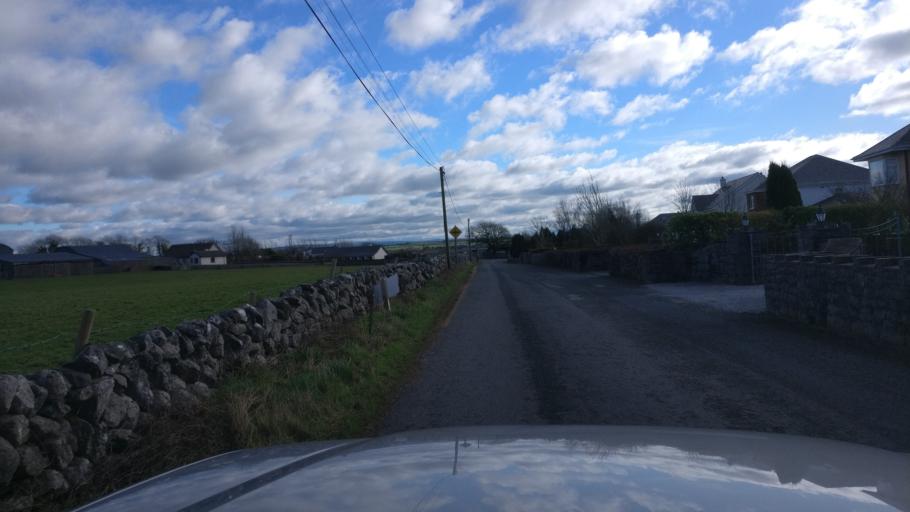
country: IE
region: Connaught
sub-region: County Galway
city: Oranmore
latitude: 53.2781
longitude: -8.8909
